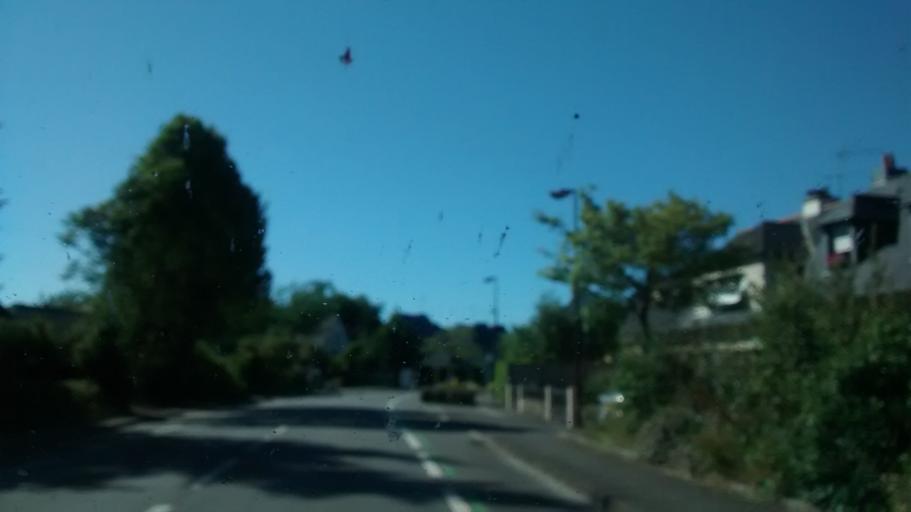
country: FR
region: Brittany
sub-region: Departement d'Ille-et-Vilaine
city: Chantepie
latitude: 48.0949
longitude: -1.6185
